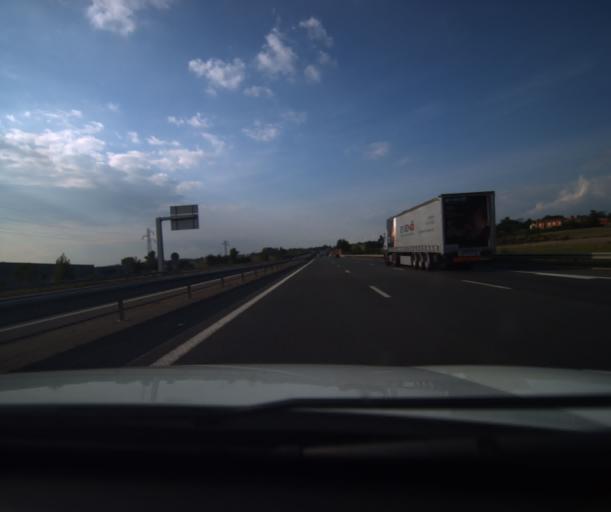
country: FR
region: Midi-Pyrenees
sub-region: Departement de la Haute-Garonne
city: Bouloc
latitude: 43.7691
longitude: 1.3849
